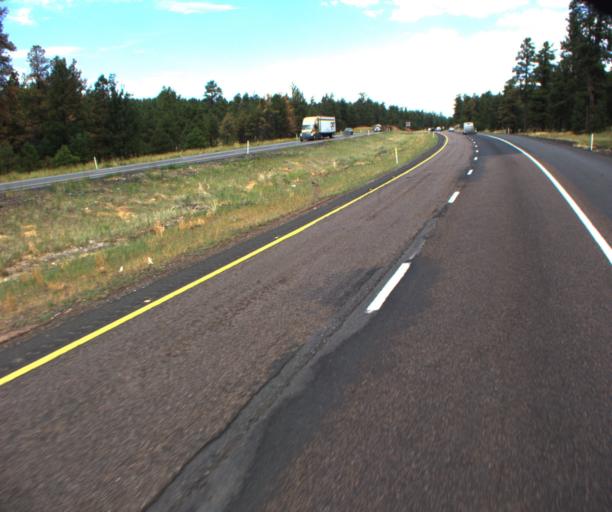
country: US
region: Arizona
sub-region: Coconino County
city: Mountainaire
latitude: 35.0735
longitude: -111.6828
